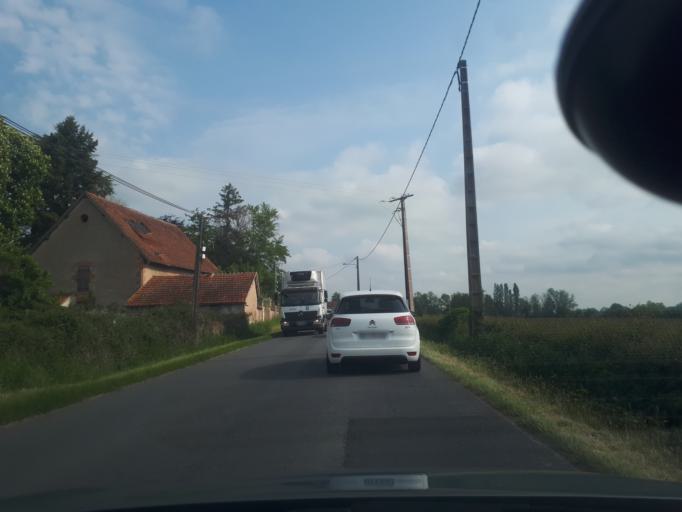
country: FR
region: Auvergne
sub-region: Departement de l'Allier
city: Lapalisse
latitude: 46.3759
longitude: 3.5833
